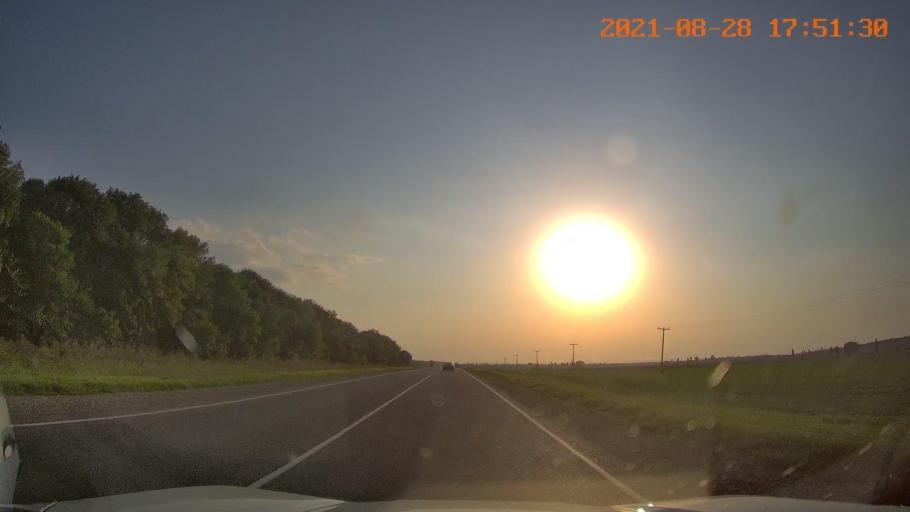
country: RU
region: Krasnodarskiy
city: Konstantinovskaya
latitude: 44.9437
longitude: 40.7924
